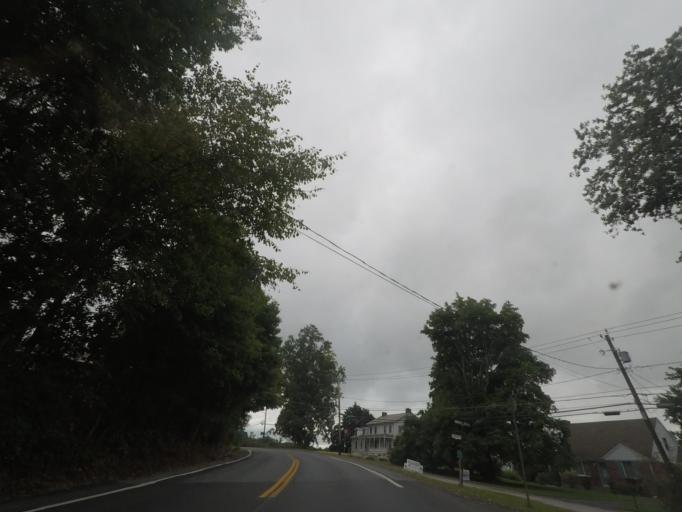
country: US
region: New York
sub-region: Rensselaer County
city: Hoosick Falls
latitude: 42.9257
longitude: -73.3466
